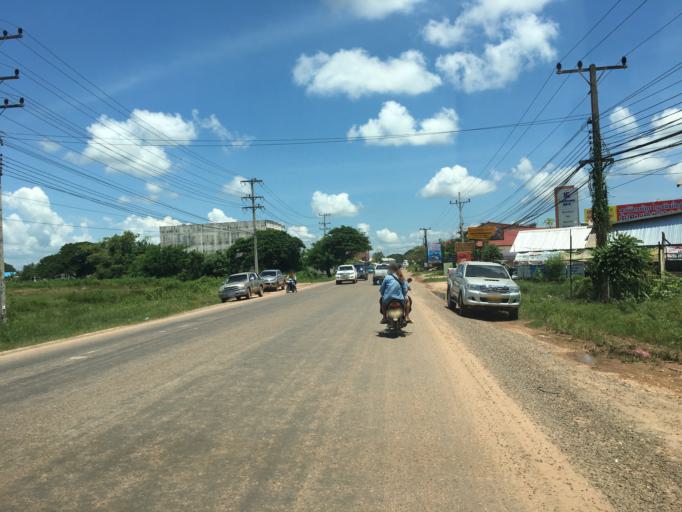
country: LA
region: Vientiane
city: Vientiane
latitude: 18.0467
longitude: 102.5458
